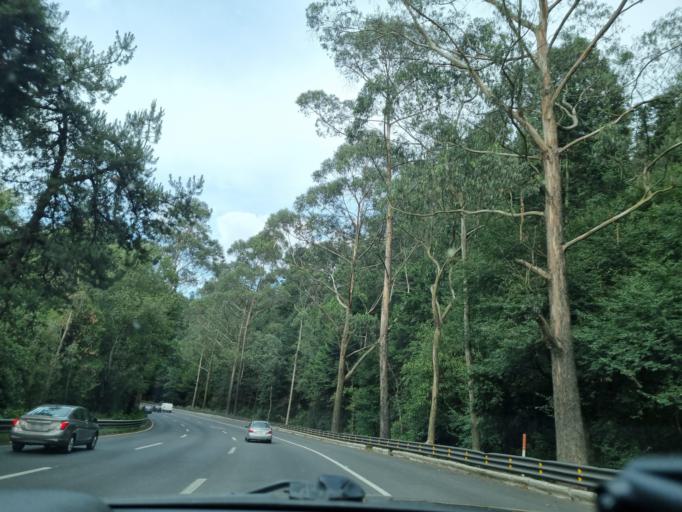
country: MX
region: Morelos
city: San Jeronimo Acazulco
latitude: 19.2919
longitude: -99.4199
